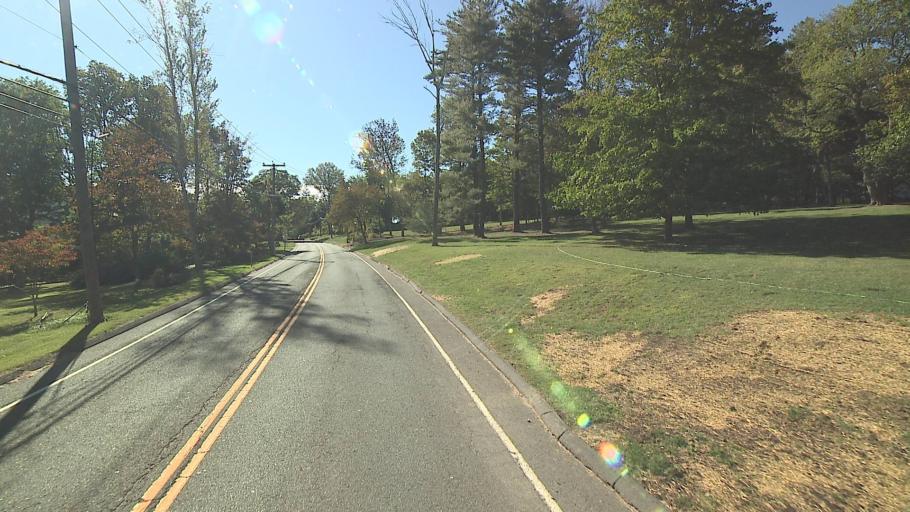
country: US
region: Connecticut
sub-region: Fairfield County
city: New Canaan
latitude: 41.1806
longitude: -73.5201
